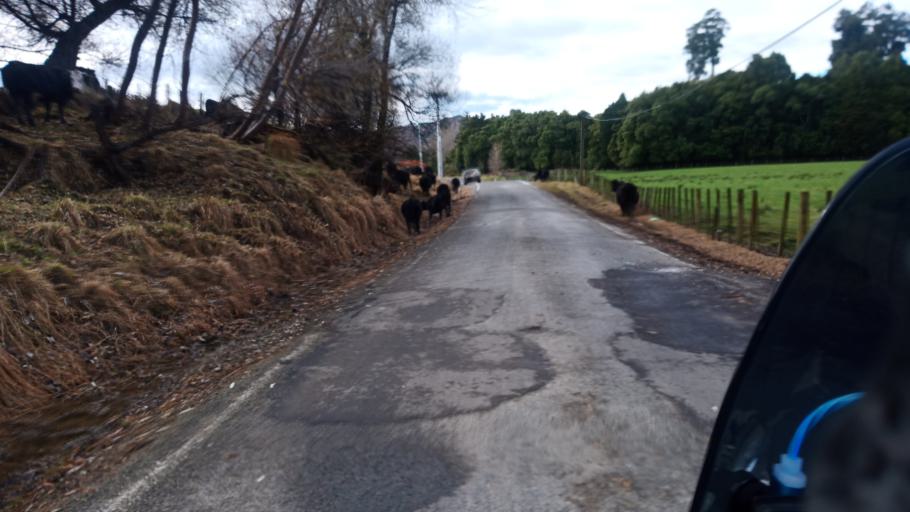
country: NZ
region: Gisborne
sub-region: Gisborne District
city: Gisborne
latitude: -38.4191
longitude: 177.9215
